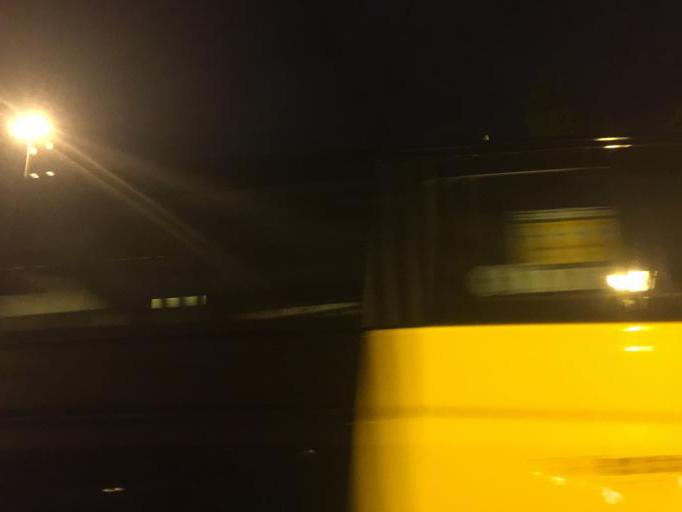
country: ES
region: Catalonia
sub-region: Provincia de Barcelona
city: les Corts
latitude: 41.3922
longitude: 2.1293
